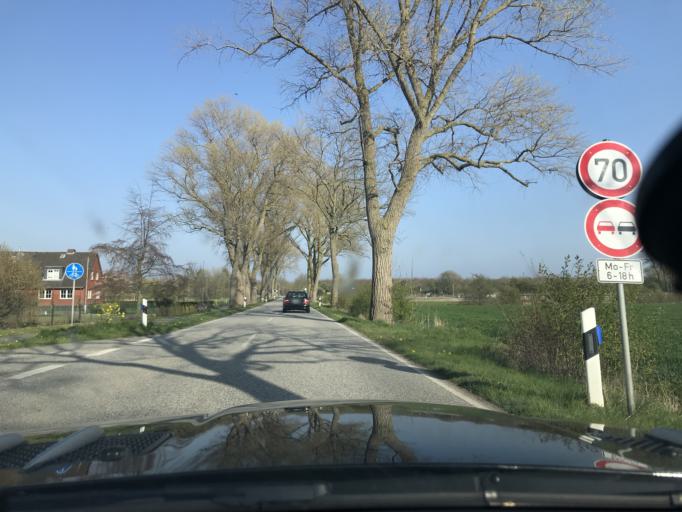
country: DE
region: Schleswig-Holstein
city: Grossenbrode
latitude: 54.3643
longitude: 11.0694
